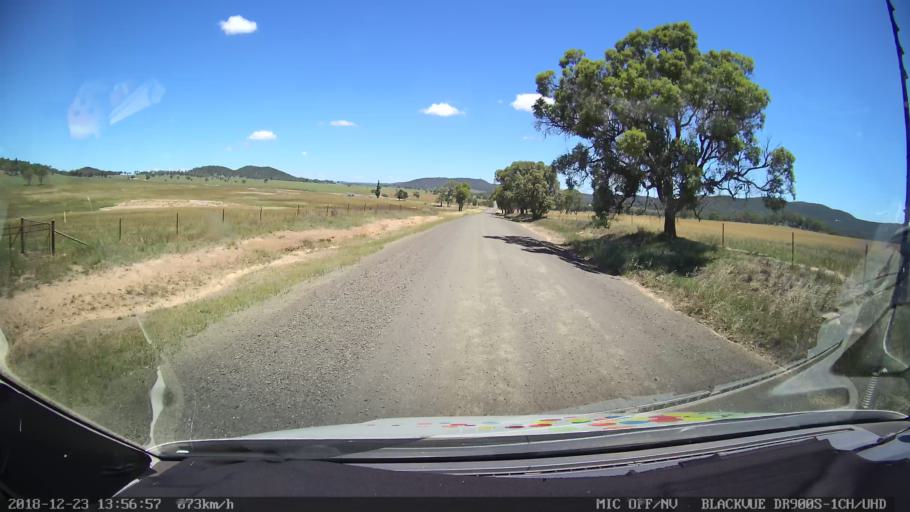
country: AU
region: New South Wales
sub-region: Tamworth Municipality
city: Manilla
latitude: -30.5826
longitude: 151.0944
